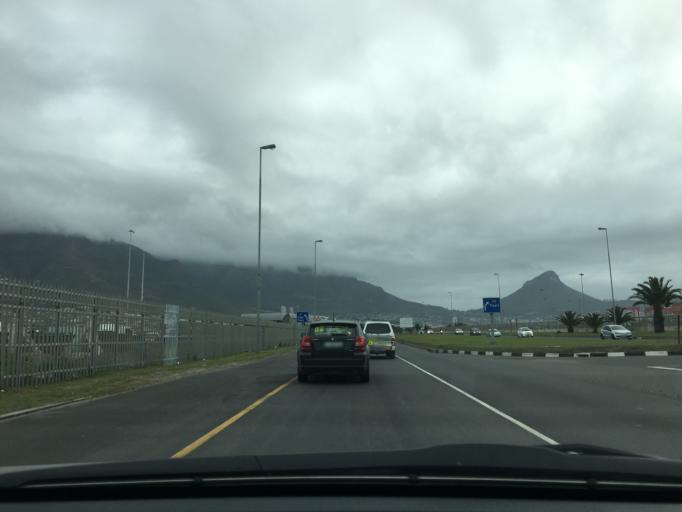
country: ZA
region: Western Cape
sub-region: City of Cape Town
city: Cape Town
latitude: -33.9187
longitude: 18.4591
